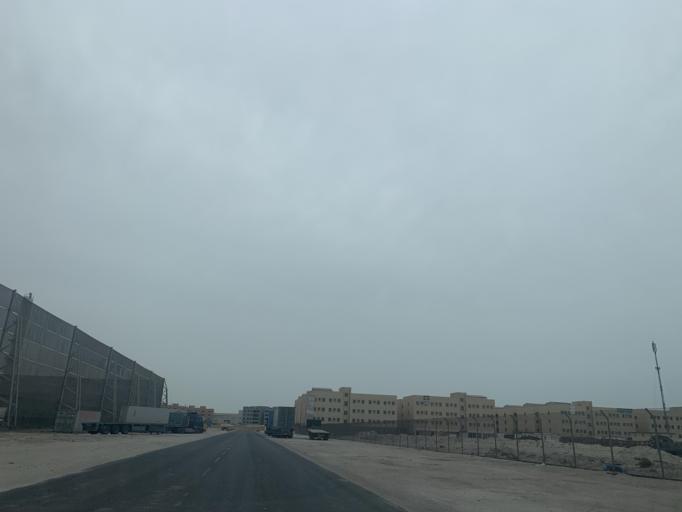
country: BH
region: Muharraq
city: Al Hadd
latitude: 26.2061
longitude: 50.6806
